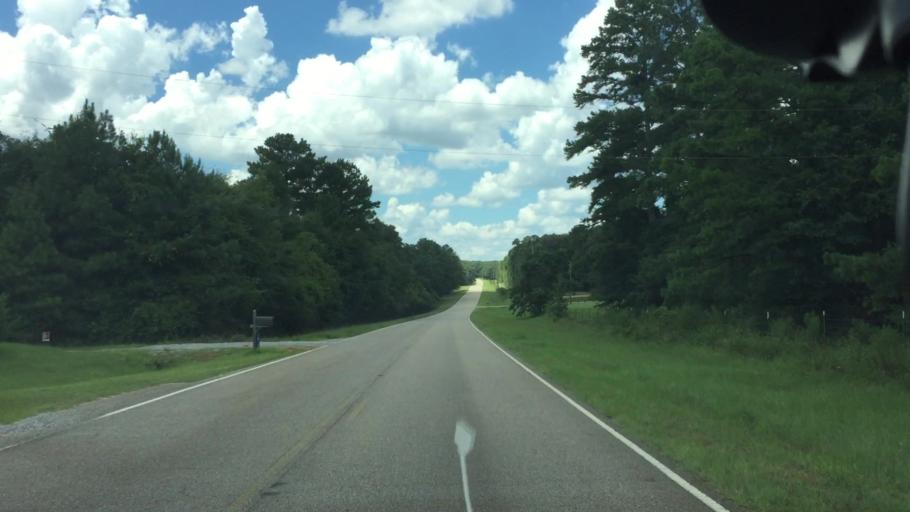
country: US
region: Alabama
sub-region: Coffee County
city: New Brockton
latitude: 31.4106
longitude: -85.8551
